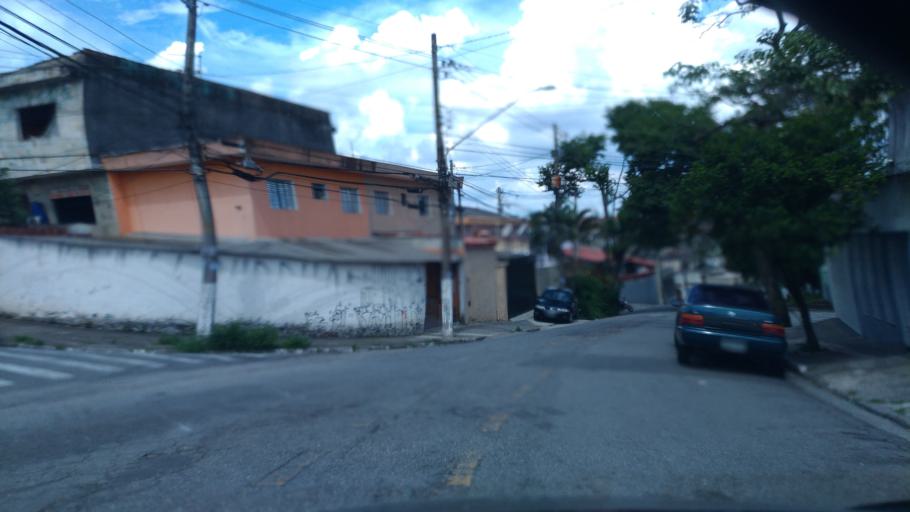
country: BR
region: Sao Paulo
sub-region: Sao Bernardo Do Campo
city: Sao Bernardo do Campo
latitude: -23.7028
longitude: -46.5836
